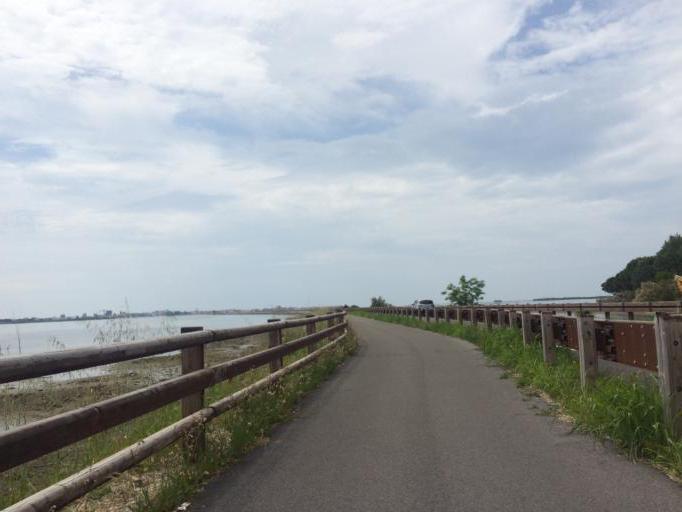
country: IT
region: Friuli Venezia Giulia
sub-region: Provincia di Gorizia
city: Grado
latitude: 45.7103
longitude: 13.3835
